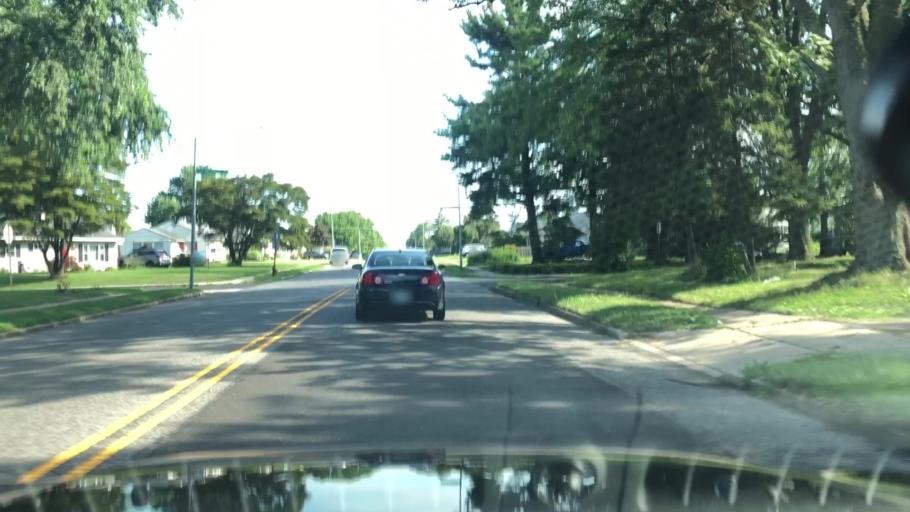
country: US
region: Pennsylvania
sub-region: Bucks County
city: Fairless Hills
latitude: 40.1893
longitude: -74.8392
